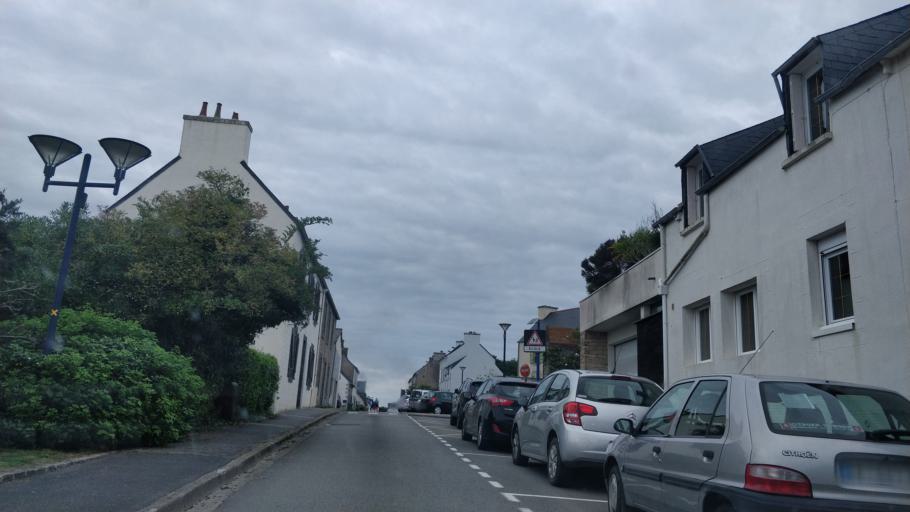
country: FR
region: Brittany
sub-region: Departement du Finistere
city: Loperhet
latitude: 48.3754
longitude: -4.3048
